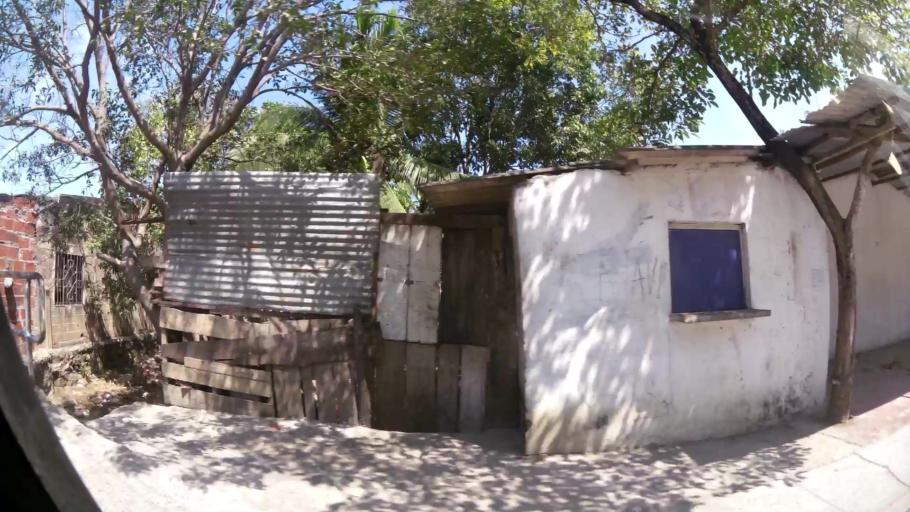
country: CO
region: Atlantico
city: Barranquilla
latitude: 10.9671
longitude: -74.8293
